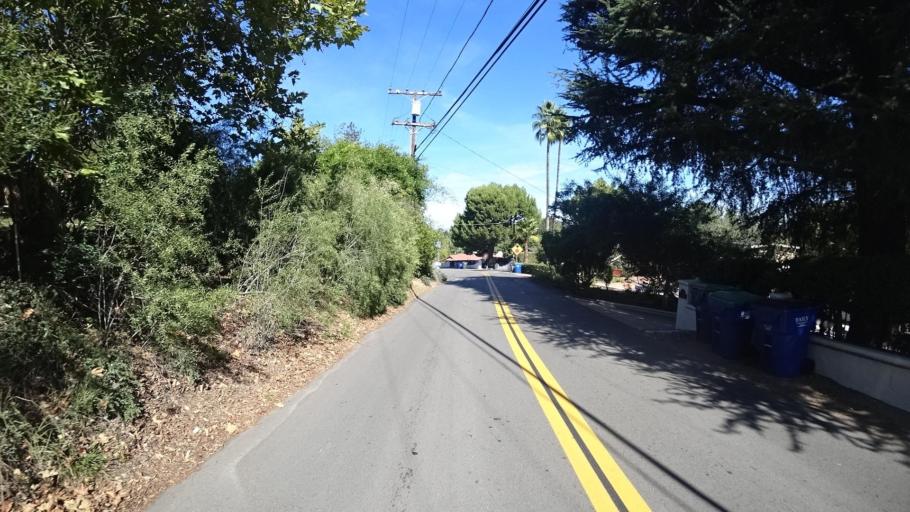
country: US
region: California
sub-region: San Diego County
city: Casa de Oro-Mount Helix
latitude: 32.7641
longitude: -116.9651
